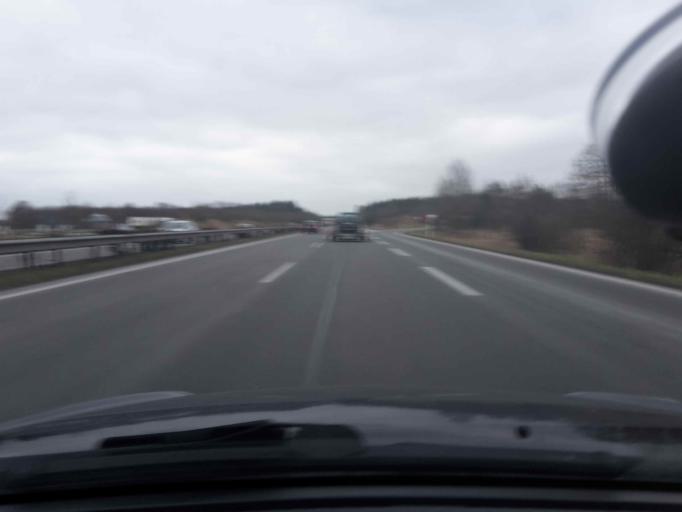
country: DE
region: Lower Saxony
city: Radbruch
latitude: 53.3307
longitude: 10.2727
